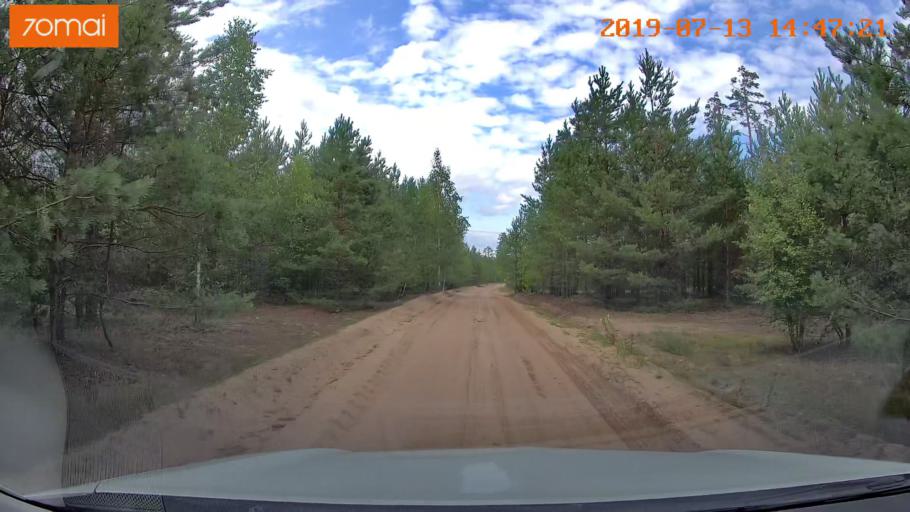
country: BY
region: Mogilev
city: Hlusha
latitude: 53.2001
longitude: 28.7538
